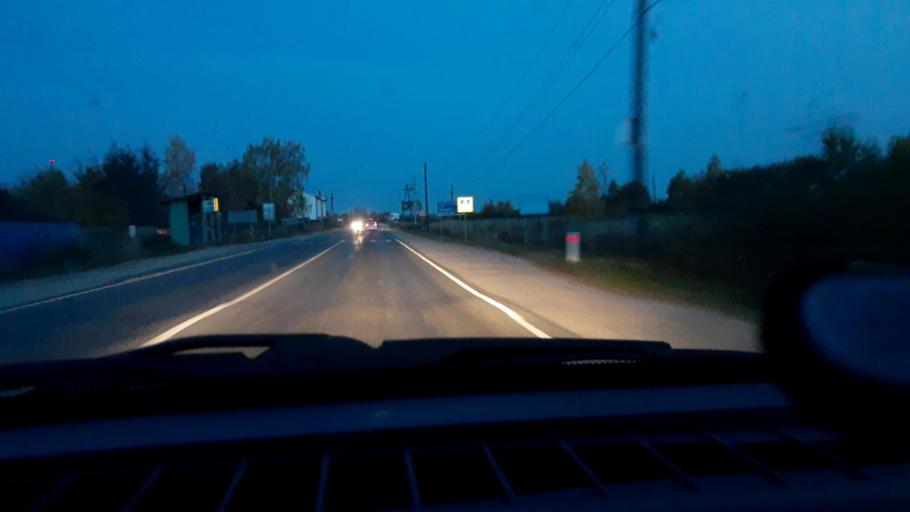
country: RU
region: Nizjnij Novgorod
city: Gorodets
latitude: 56.6400
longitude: 43.5031
